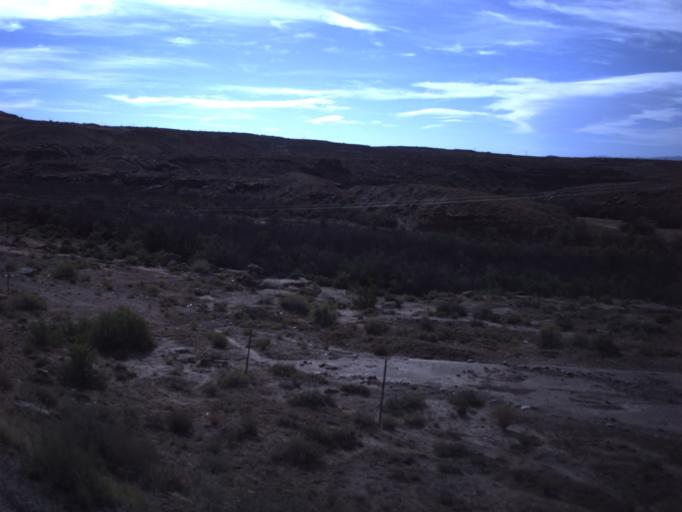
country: US
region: Utah
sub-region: San Juan County
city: Blanding
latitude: 37.3086
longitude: -109.2977
